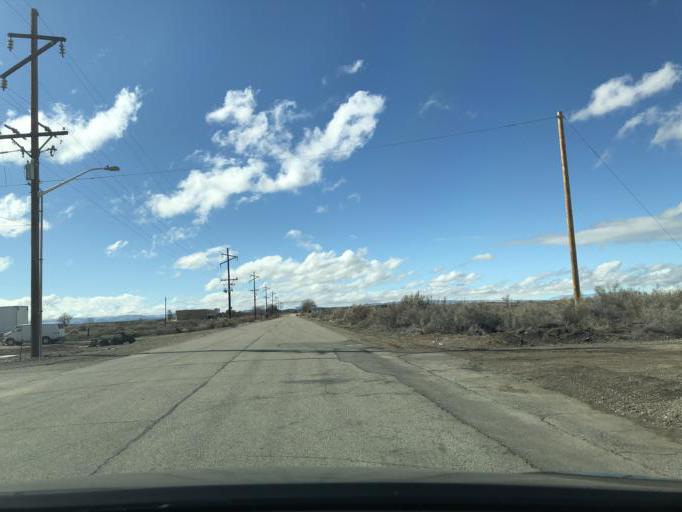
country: US
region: Utah
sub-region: Carbon County
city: East Carbon City
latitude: 39.0007
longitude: -110.1650
